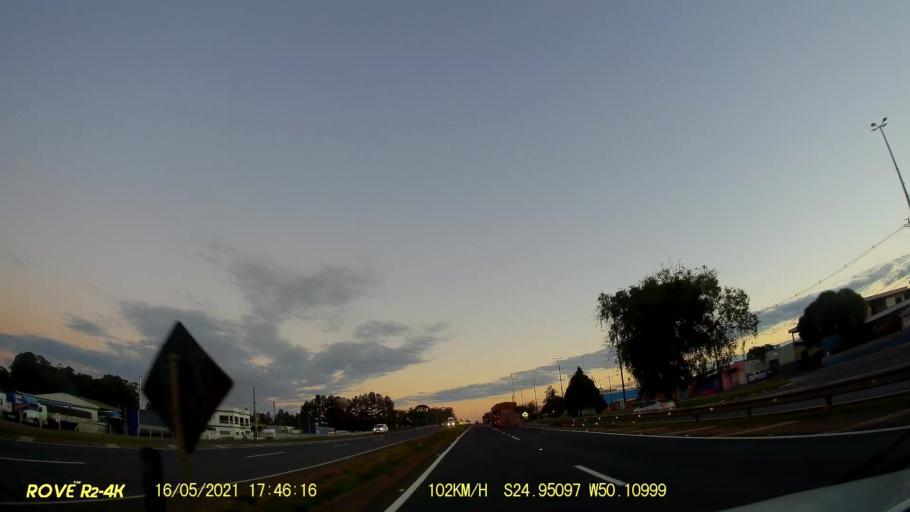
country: BR
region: Parana
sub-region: Carambei
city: Carambei
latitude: -24.9512
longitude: -50.1100
